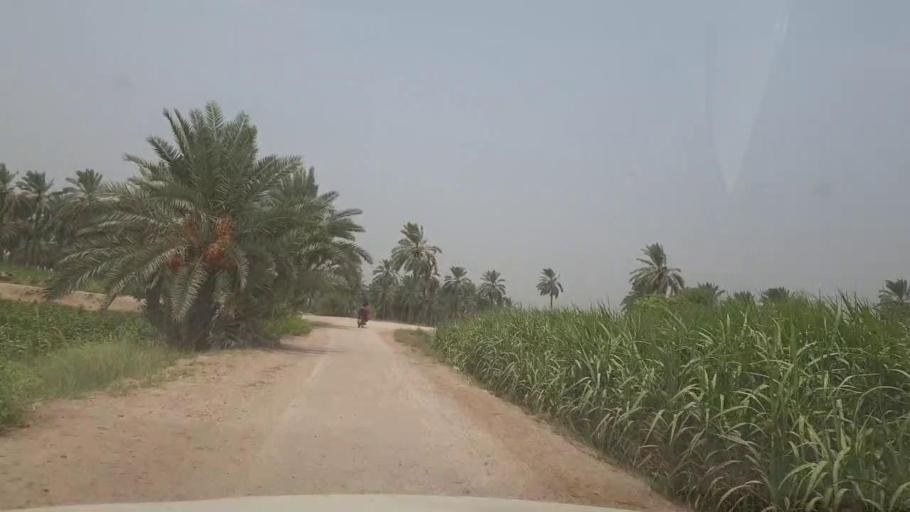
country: PK
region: Sindh
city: Kot Diji
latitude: 27.4430
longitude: 68.6398
